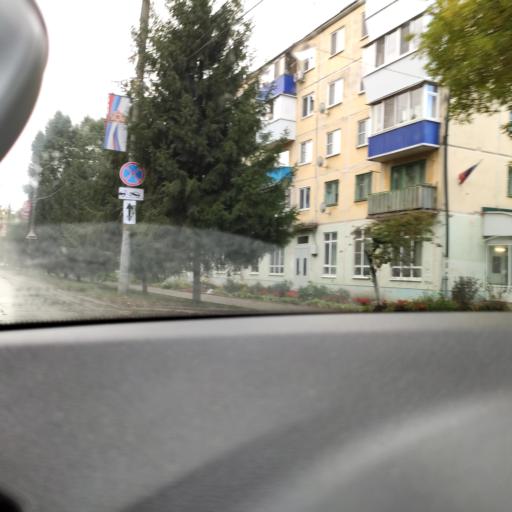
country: RU
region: Samara
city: Novosemeykino
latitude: 53.3709
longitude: 50.3550
